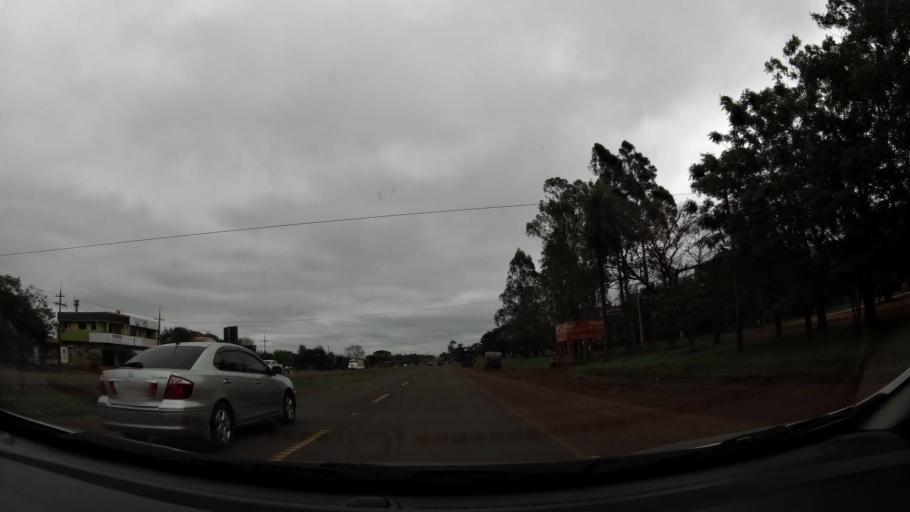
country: PY
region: Alto Parana
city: Presidente Franco
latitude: -25.4898
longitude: -54.7866
